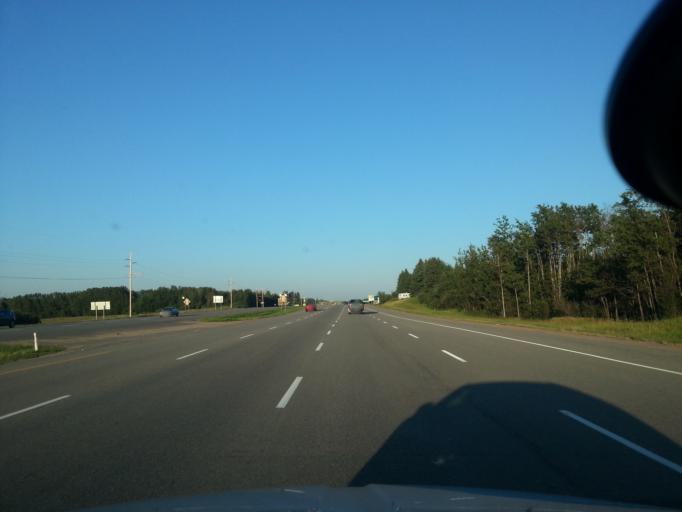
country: CA
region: Alberta
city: Stony Plain
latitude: 53.5700
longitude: -114.2126
